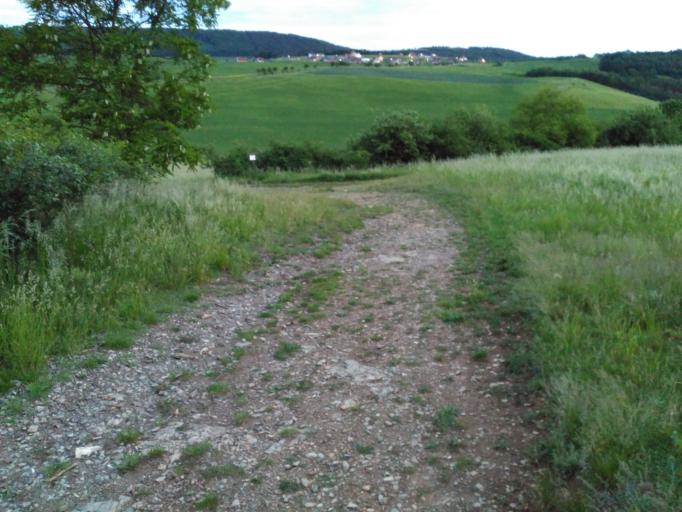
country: CZ
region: Central Bohemia
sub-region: Okres Beroun
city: Kraluv Dvur
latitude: 49.9181
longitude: 14.0269
